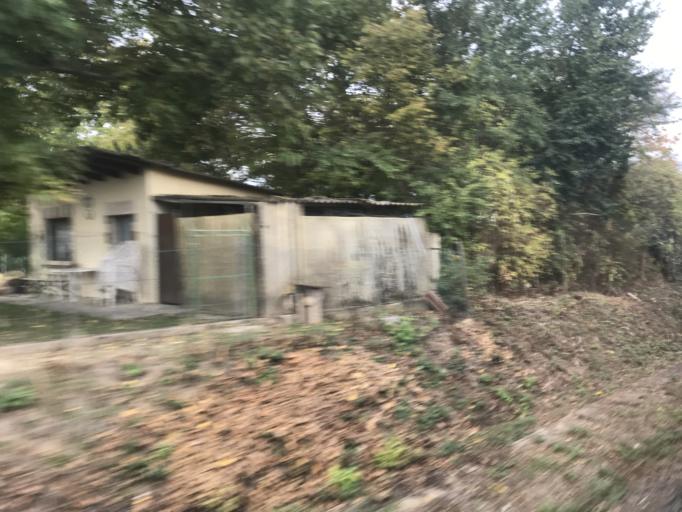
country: DE
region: Rheinland-Pfalz
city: Armsheim
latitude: 49.8107
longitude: 8.0720
